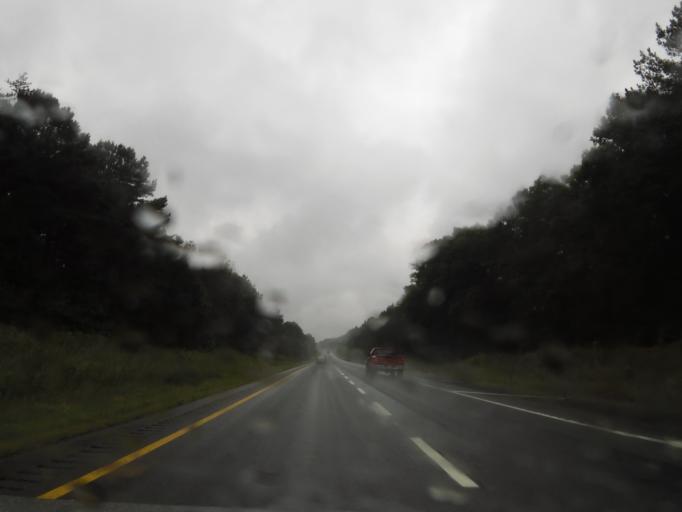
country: US
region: Tennessee
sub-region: Bradley County
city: Hopewell
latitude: 35.2642
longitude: -84.8311
